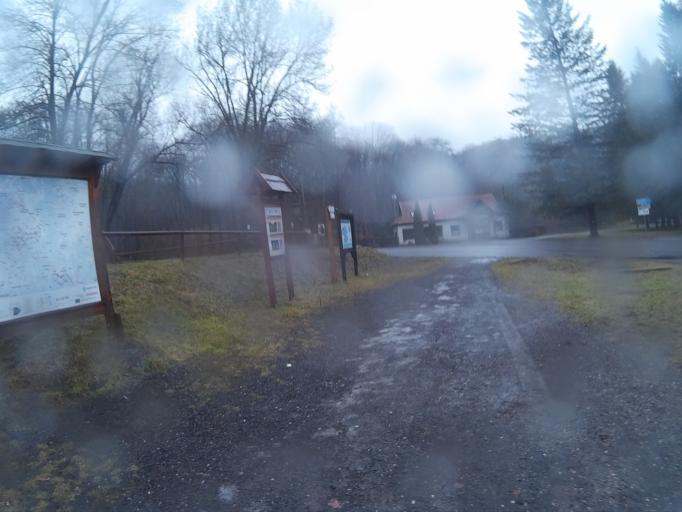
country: HU
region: Nograd
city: Somoskoujfalu
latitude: 48.1556
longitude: 19.8523
